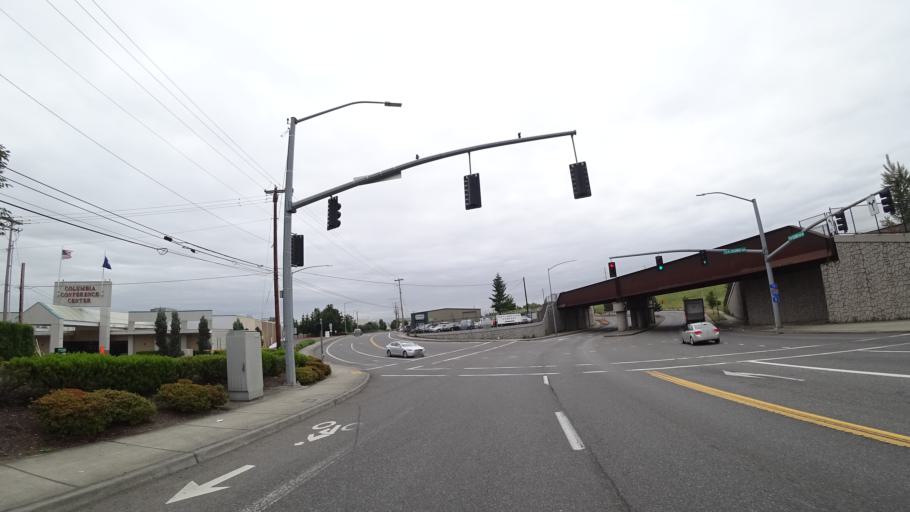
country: US
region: Oregon
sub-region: Multnomah County
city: Lents
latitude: 45.5644
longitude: -122.5757
